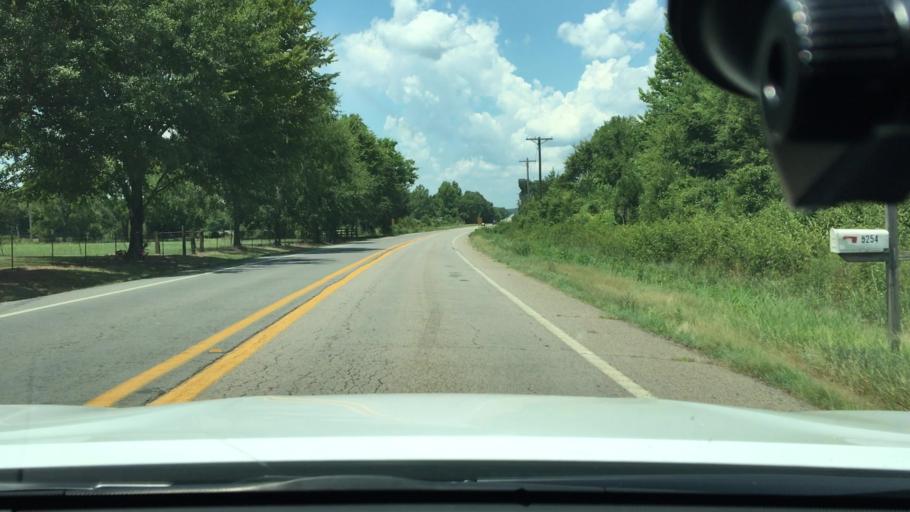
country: US
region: Arkansas
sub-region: Logan County
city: Booneville
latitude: 35.1475
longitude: -93.8403
